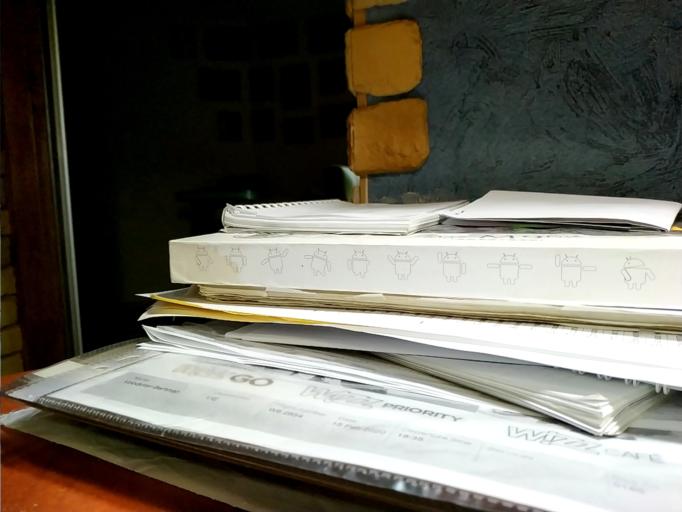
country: RU
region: Arkhangelskaya
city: Onega
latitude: 63.6191
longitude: 38.0755
